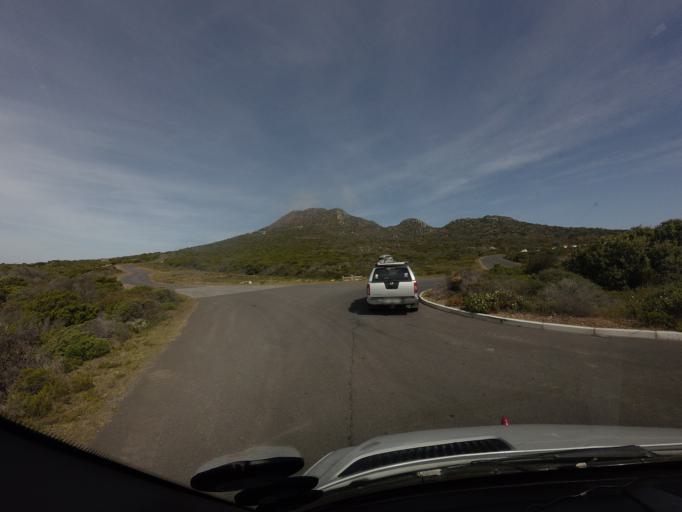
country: ZA
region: Western Cape
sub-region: City of Cape Town
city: Retreat
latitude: -34.3413
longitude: 18.4673
